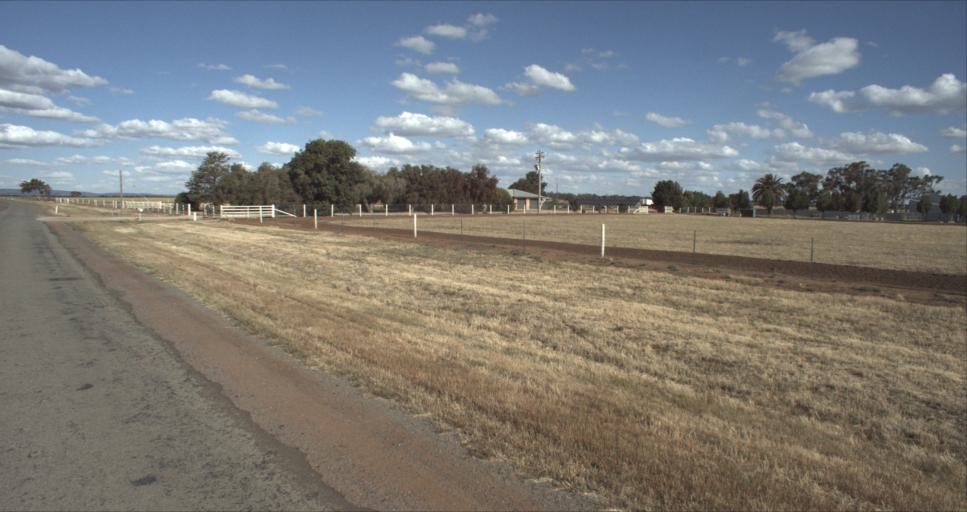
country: AU
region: New South Wales
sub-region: Leeton
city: Leeton
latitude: -34.4565
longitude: 146.2865
